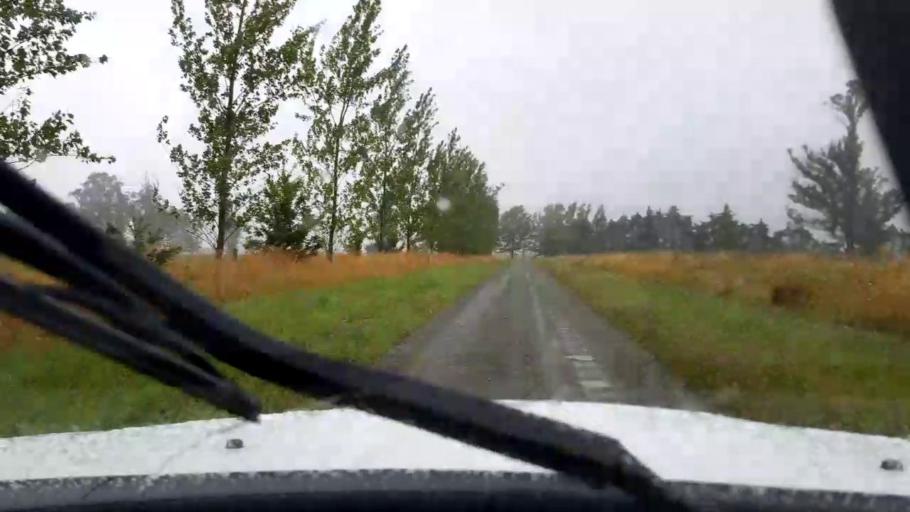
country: NZ
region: Canterbury
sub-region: Timaru District
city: Pleasant Point
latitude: -44.2014
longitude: 171.0899
